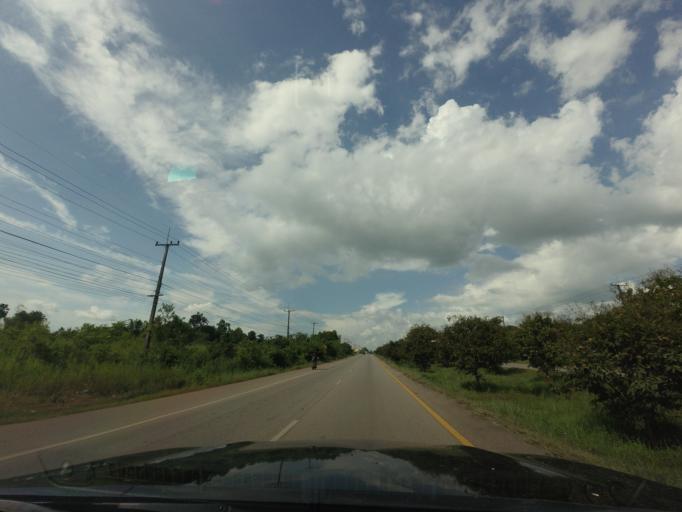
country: TH
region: Nong Khai
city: Sa Khrai
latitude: 17.5637
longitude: 102.8014
